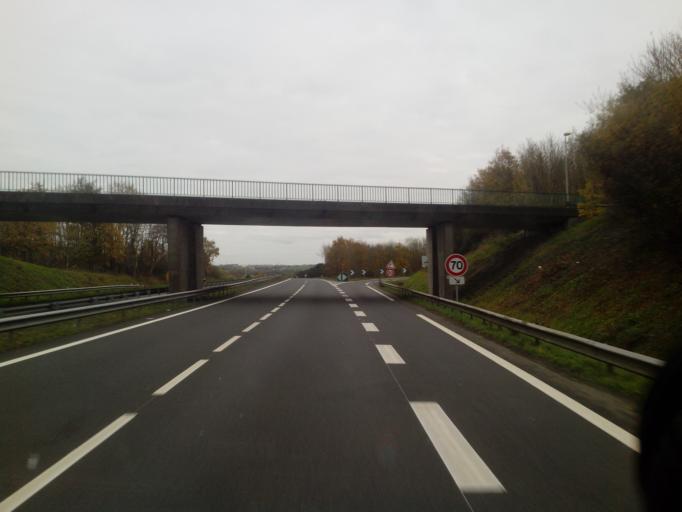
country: FR
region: Pays de la Loire
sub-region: Departement de Maine-et-Loire
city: Saint-Andre-de-la-Marche
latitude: 47.0936
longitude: -1.0073
